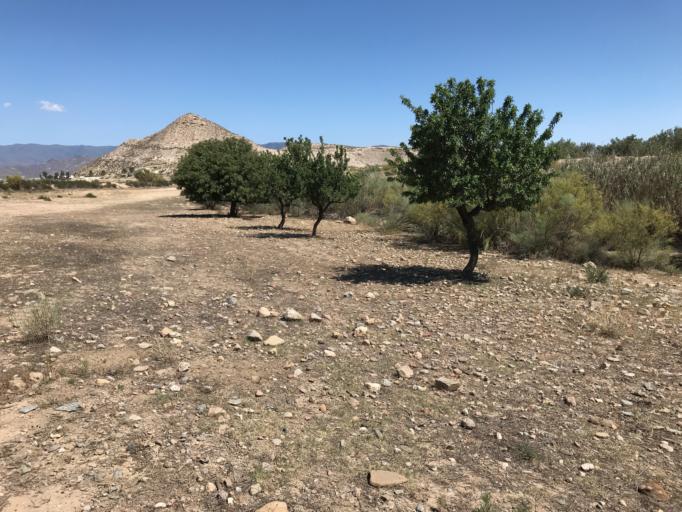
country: ES
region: Andalusia
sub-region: Provincia de Almeria
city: Turrillas
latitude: 37.0719
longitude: -2.2953
